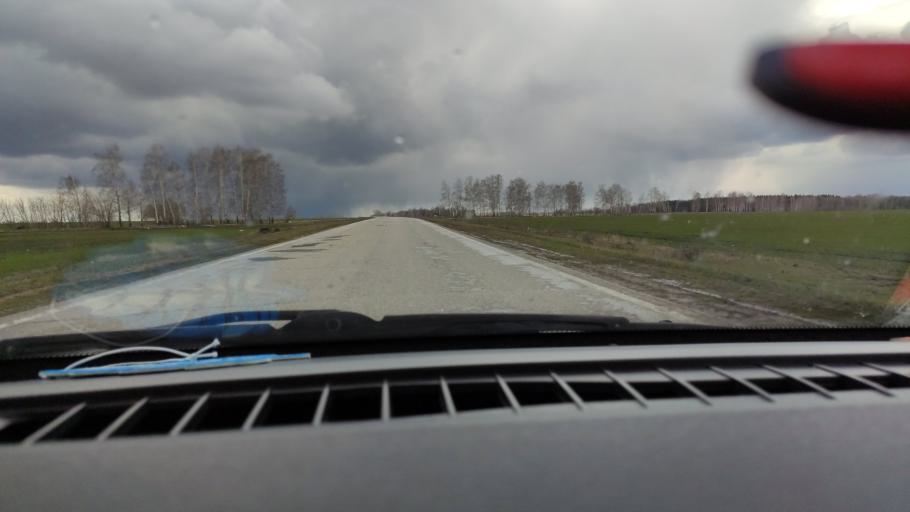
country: RU
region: Samara
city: Povolzhskiy
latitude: 53.8007
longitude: 49.7781
